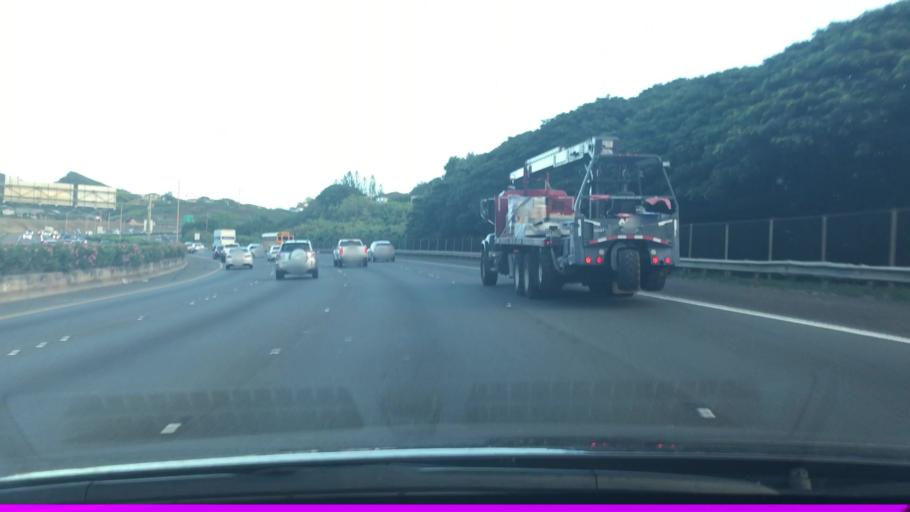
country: US
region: Hawaii
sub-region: Honolulu County
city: Halawa Heights
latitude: 21.3538
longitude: -157.8964
